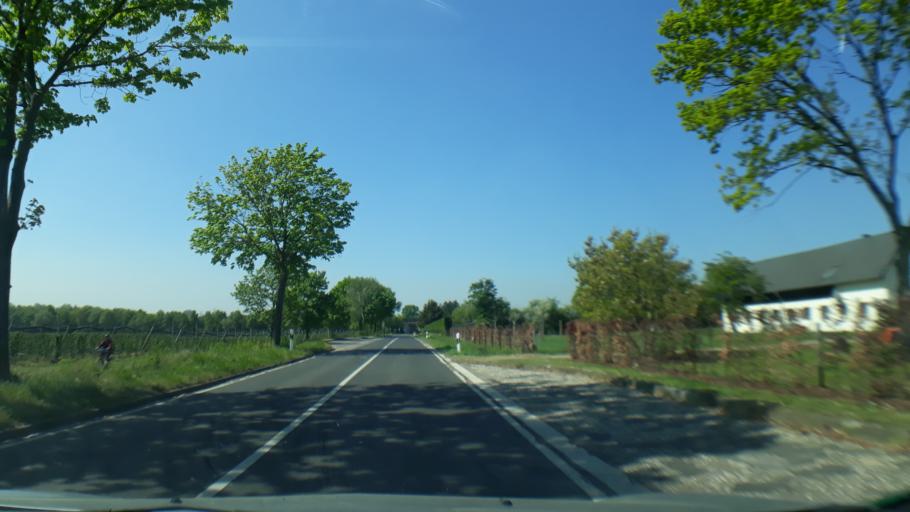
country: DE
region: North Rhine-Westphalia
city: Zulpich
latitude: 50.6970
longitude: 6.6972
